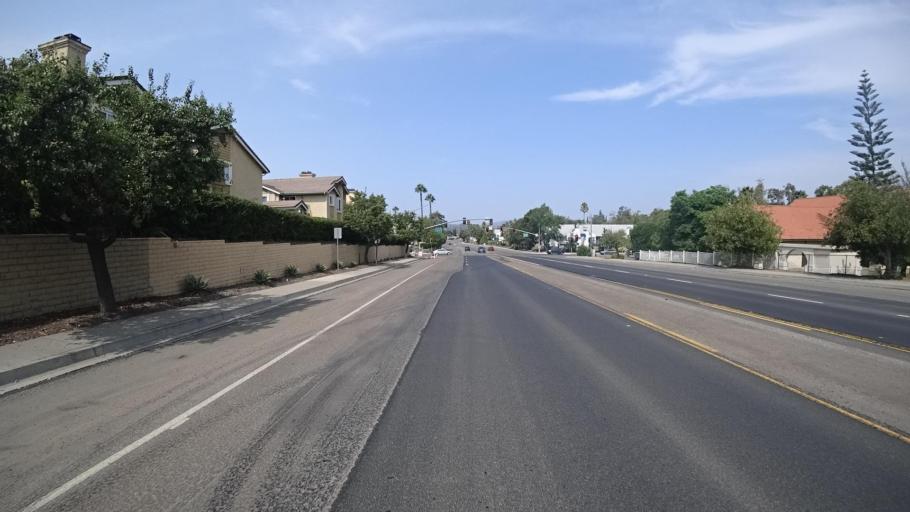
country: US
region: California
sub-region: San Diego County
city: Escondido
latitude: 33.1234
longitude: -117.0624
